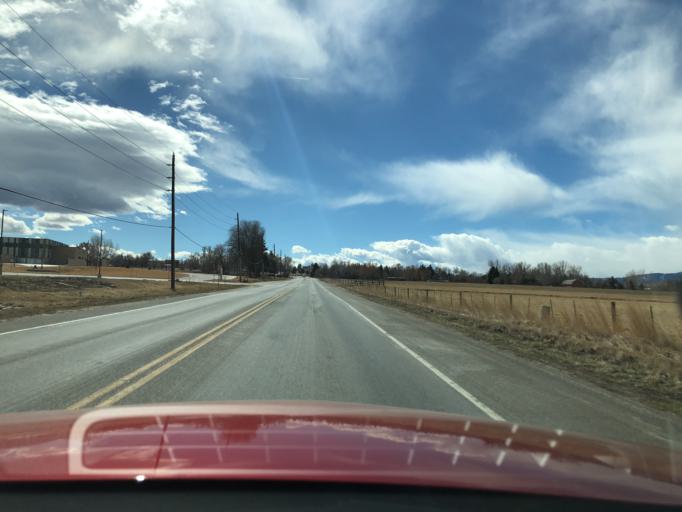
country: US
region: Colorado
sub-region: Boulder County
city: Superior
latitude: 40.0047
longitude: -105.1783
